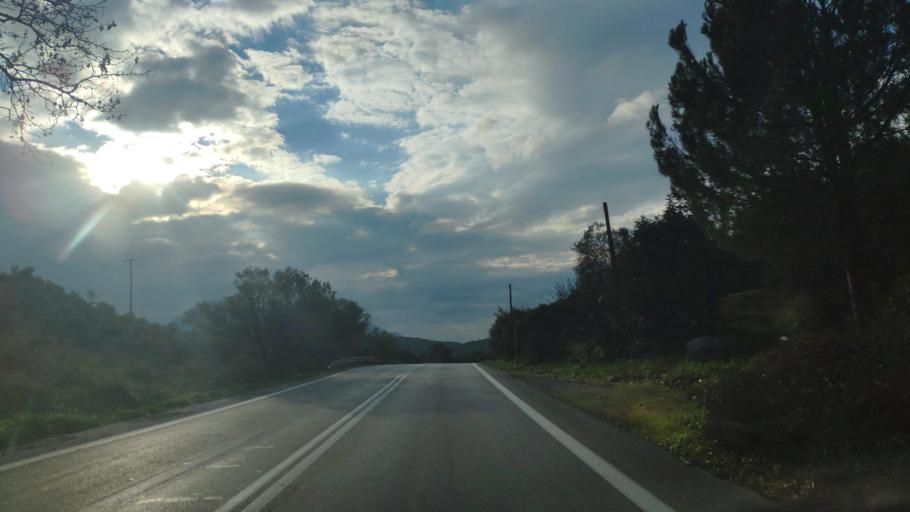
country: GR
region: Peloponnese
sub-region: Nomos Korinthias
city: Nemea
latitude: 37.7810
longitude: 22.7224
